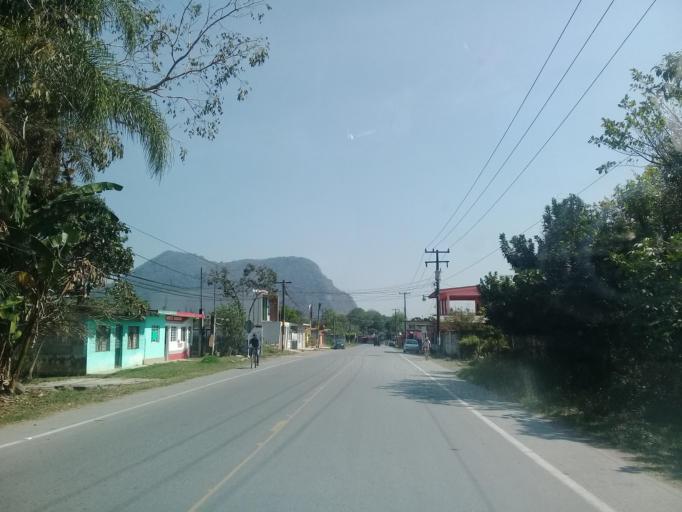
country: MX
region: Veracruz
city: Rafael Delgado
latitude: 18.7888
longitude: -97.0095
